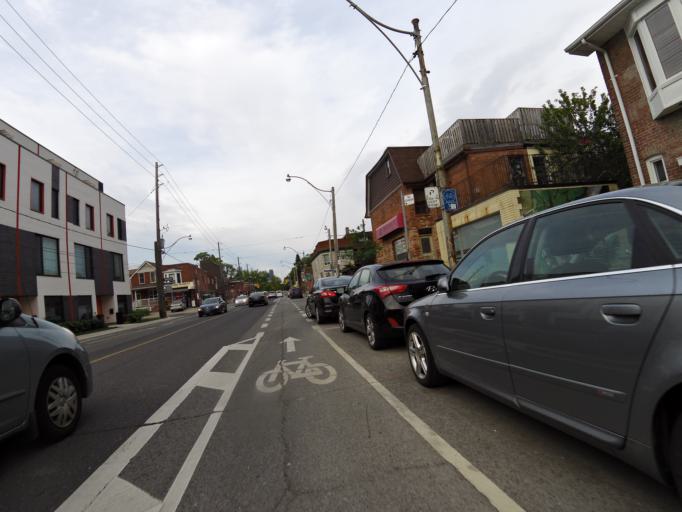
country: CA
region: Ontario
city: Toronto
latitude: 43.6591
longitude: -79.4212
